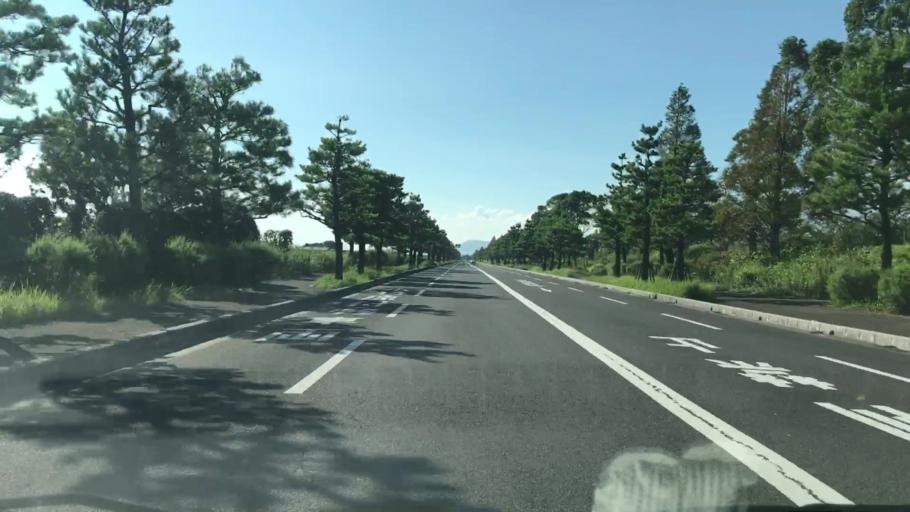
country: JP
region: Saga Prefecture
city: Okawa
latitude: 33.1553
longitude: 130.3018
